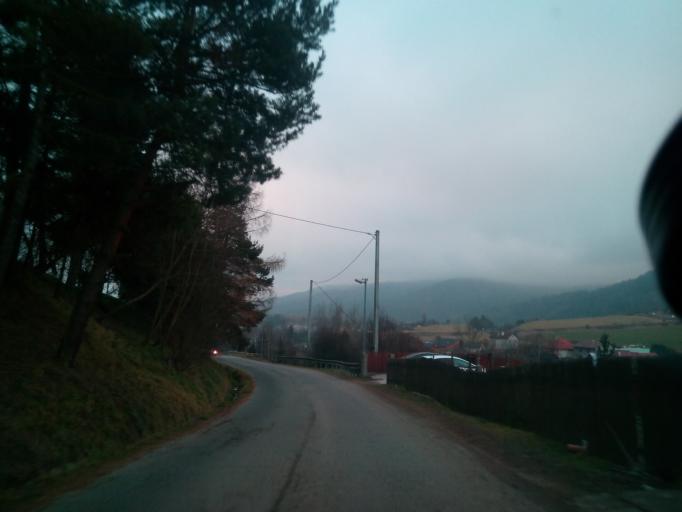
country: SK
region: Kosicky
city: Krompachy
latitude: 48.9254
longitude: 20.9275
